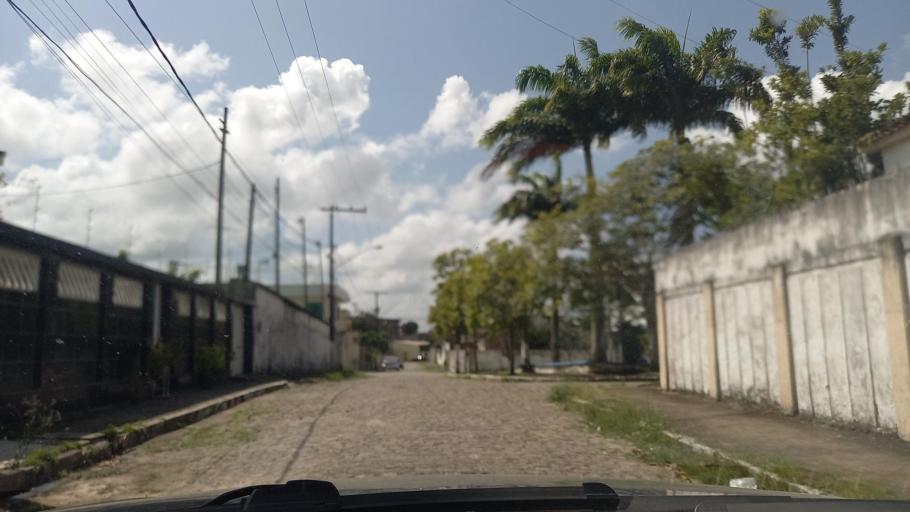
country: BR
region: Pernambuco
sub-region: Goiana
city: Goiana
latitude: -7.5697
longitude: -34.9973
